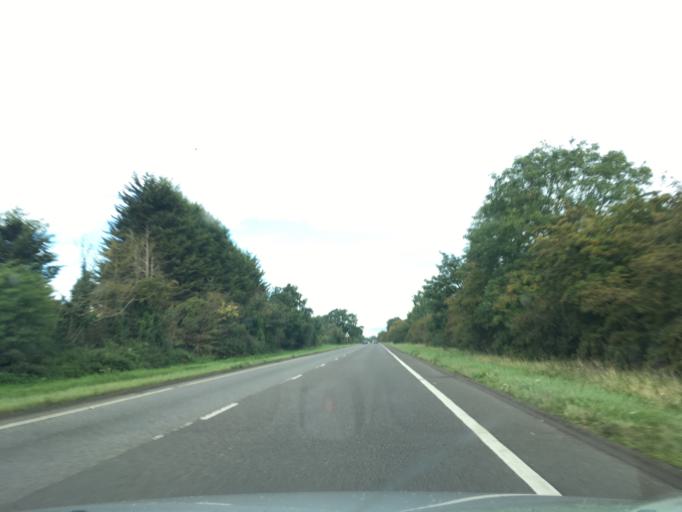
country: GB
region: England
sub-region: Oxfordshire
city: Oxford
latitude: 51.7788
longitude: -1.2373
